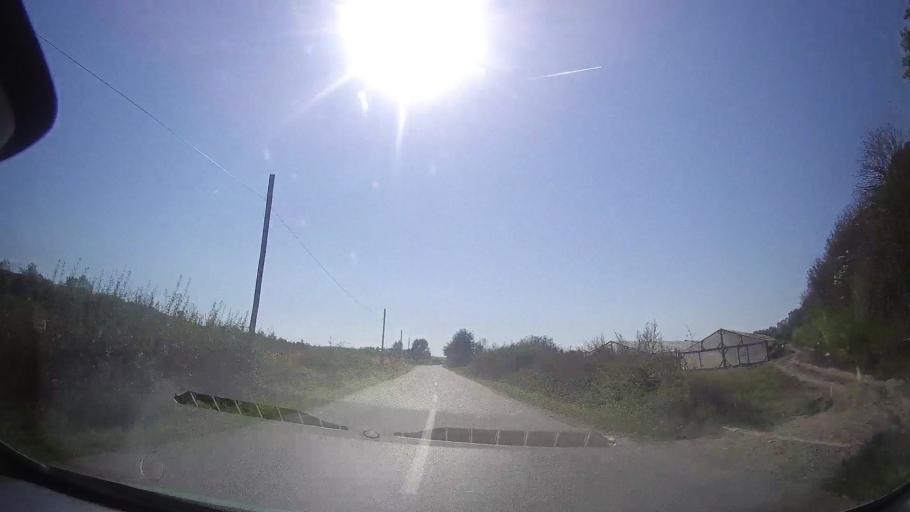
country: RO
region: Timis
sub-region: Comuna Ohaba Lunga
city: Ohaba Lunga
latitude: 45.8809
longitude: 21.9643
